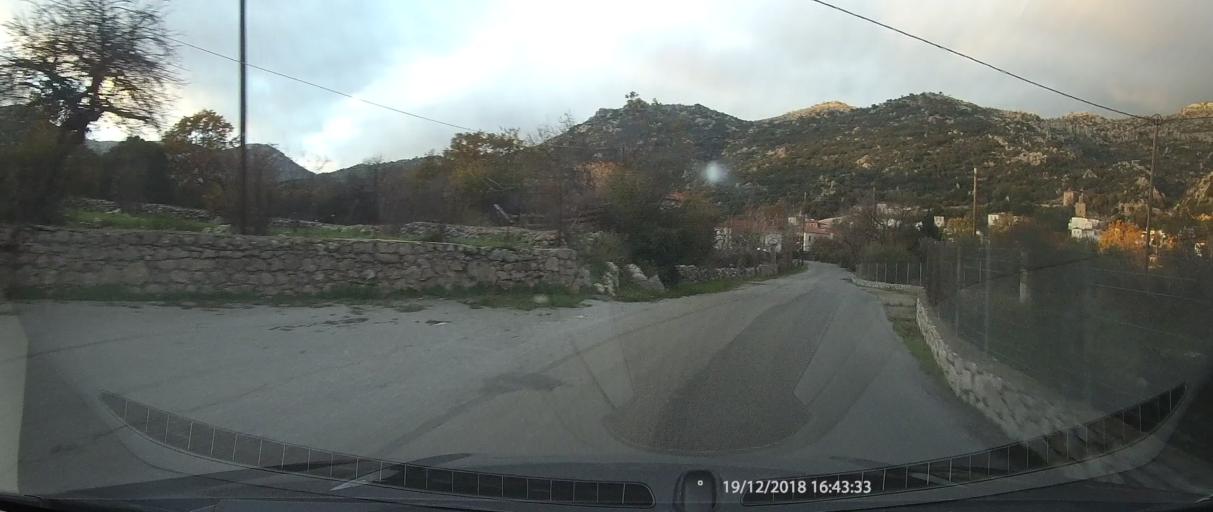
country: GR
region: Peloponnese
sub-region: Nomos Lakonias
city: Sykea
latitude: 36.9131
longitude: 22.9968
